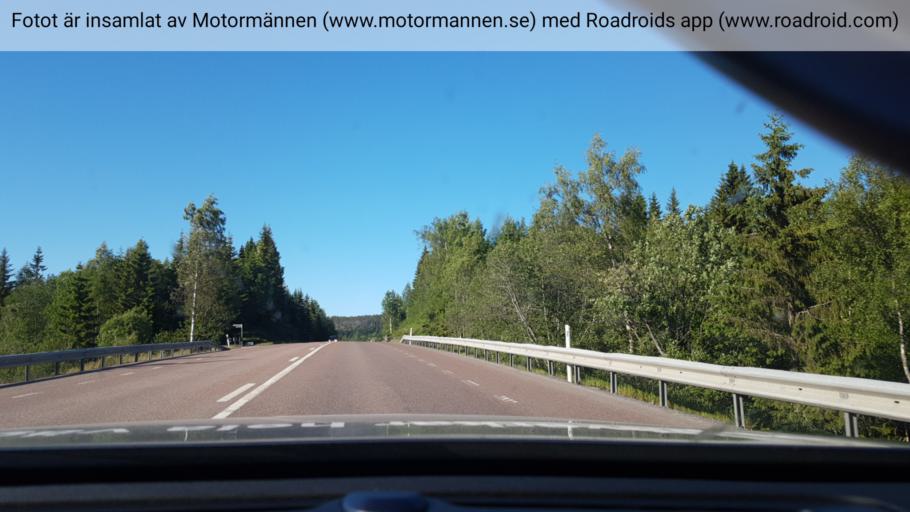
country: SE
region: Vaesternorrland
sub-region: Haernoesands Kommun
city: Haernoesand
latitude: 62.6986
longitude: 17.8550
